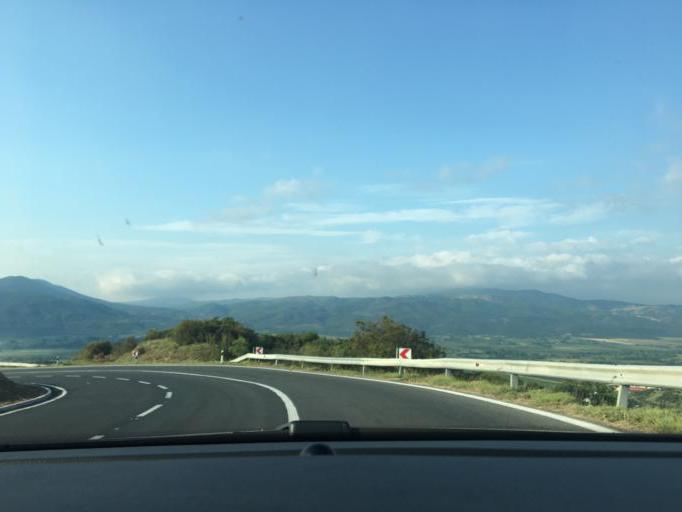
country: MK
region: Valandovo
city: Valandovo
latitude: 41.3249
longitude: 22.5960
